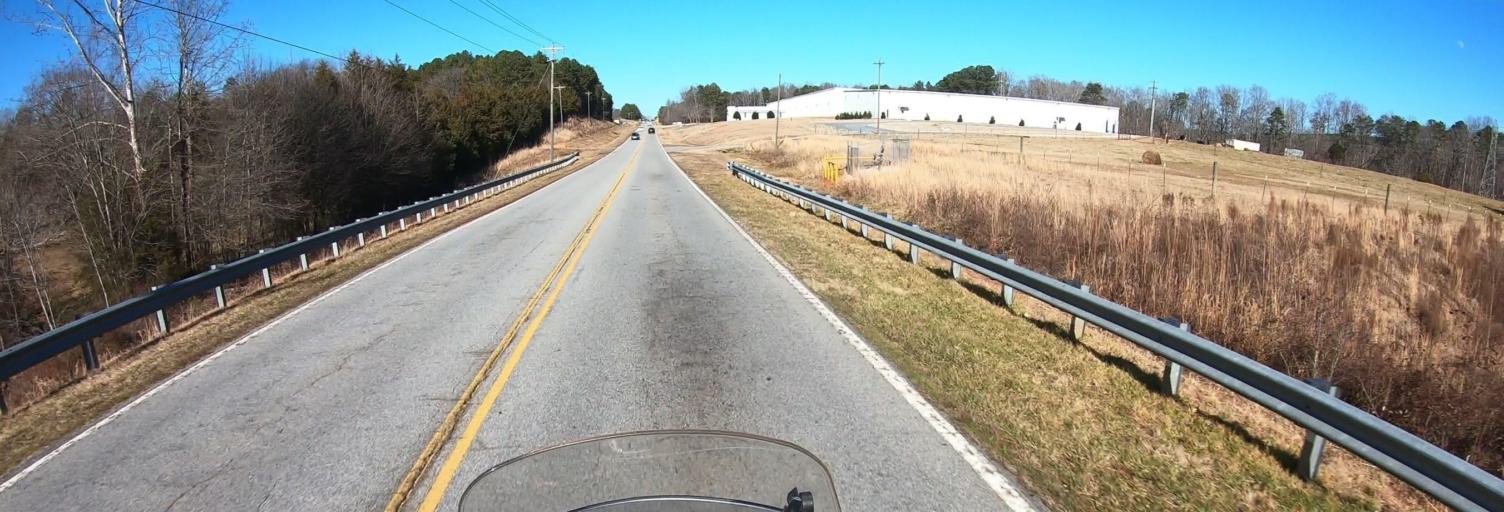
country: US
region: South Carolina
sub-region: Oconee County
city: Walhalla
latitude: 34.7343
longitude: -83.0555
